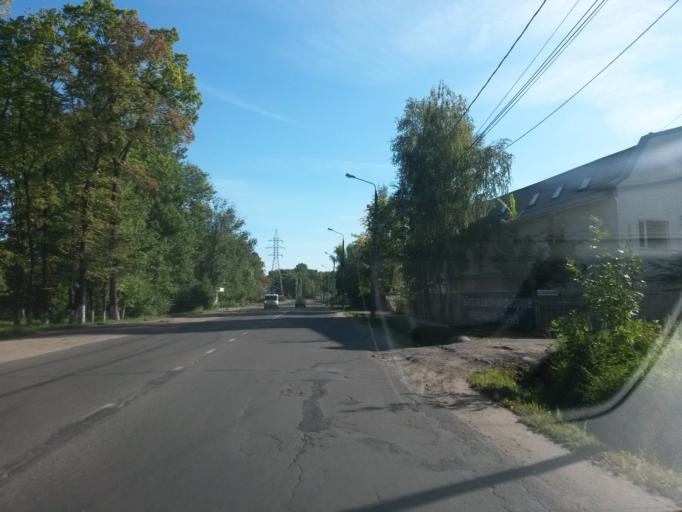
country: RU
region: Jaroslavl
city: Yaroslavl
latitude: 57.5901
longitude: 39.8772
